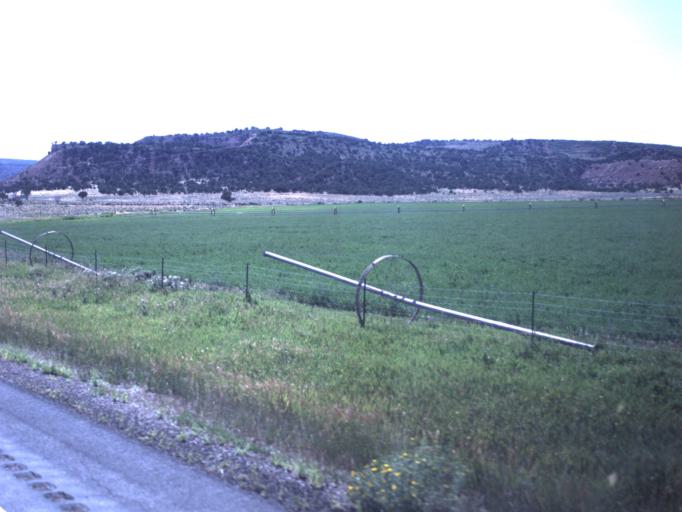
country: US
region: Utah
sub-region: Duchesne County
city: Duchesne
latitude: 40.2062
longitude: -110.8732
